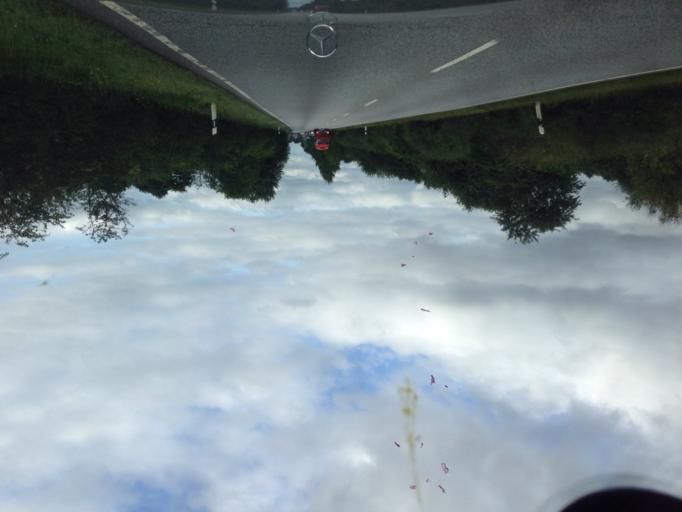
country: DE
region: Schleswig-Holstein
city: Padenstedt
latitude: 54.0432
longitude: 9.9484
